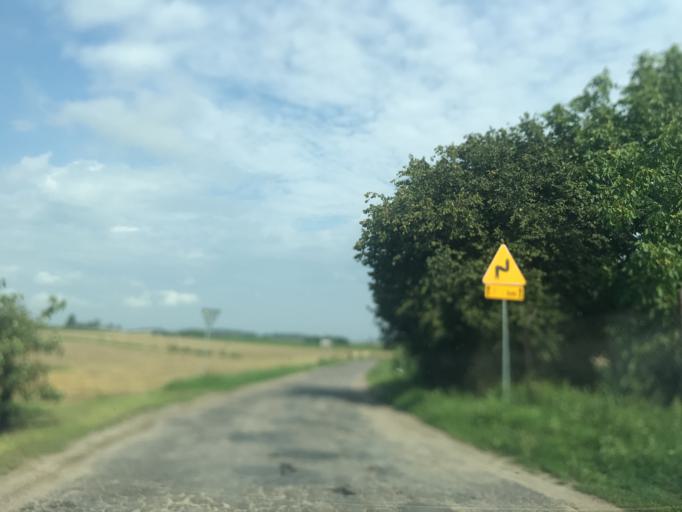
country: PL
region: Kujawsko-Pomorskie
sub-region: Powiat brodnicki
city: Brzozie
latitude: 53.3547
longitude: 19.6022
